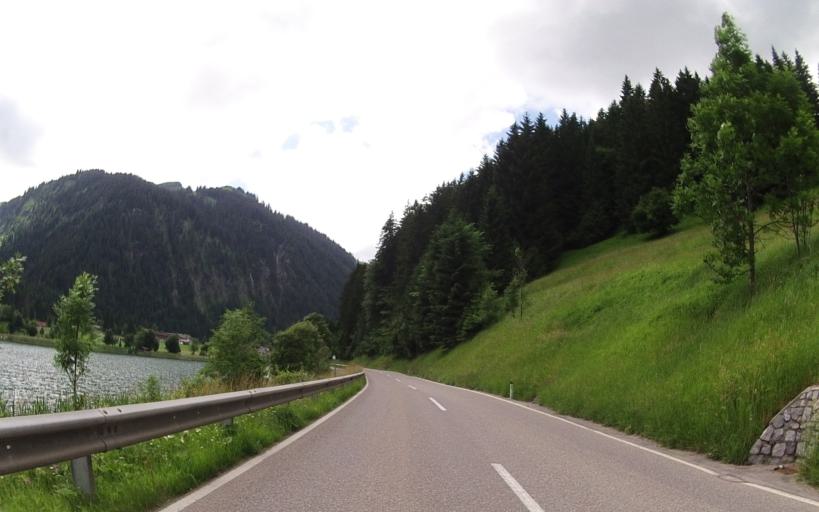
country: AT
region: Tyrol
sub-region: Politischer Bezirk Reutte
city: Graen
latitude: 47.4938
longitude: 10.5704
